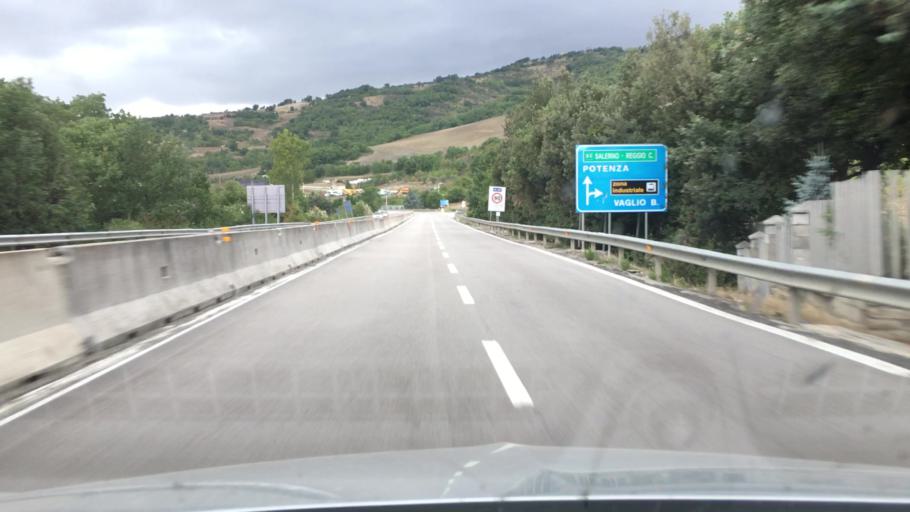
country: IT
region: Basilicate
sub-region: Provincia di Potenza
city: Vaglio Basilicata
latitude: 40.6498
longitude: 15.9300
